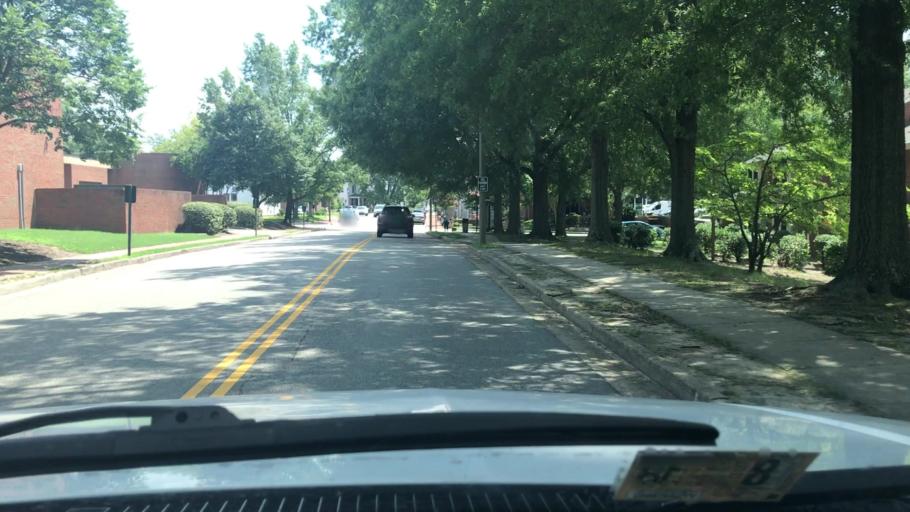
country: US
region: Virginia
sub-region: City of Williamsburg
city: Williamsburg
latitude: 37.2744
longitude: -76.7090
